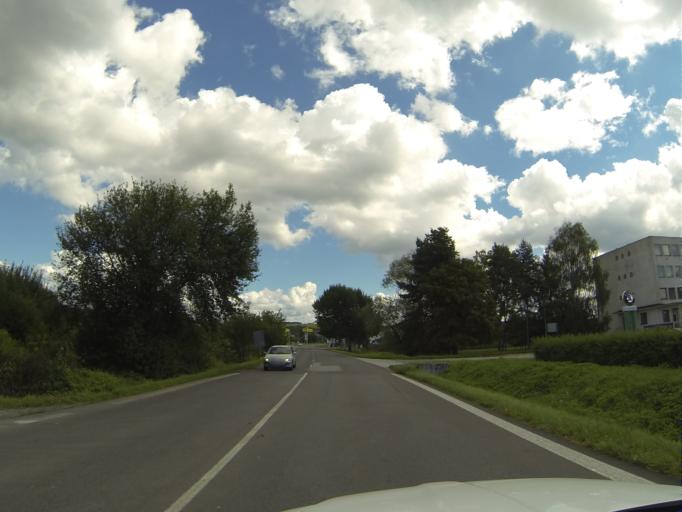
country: SK
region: Banskobystricky
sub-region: Okres Banska Bystrica
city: Zvolen
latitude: 48.5832
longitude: 19.1211
